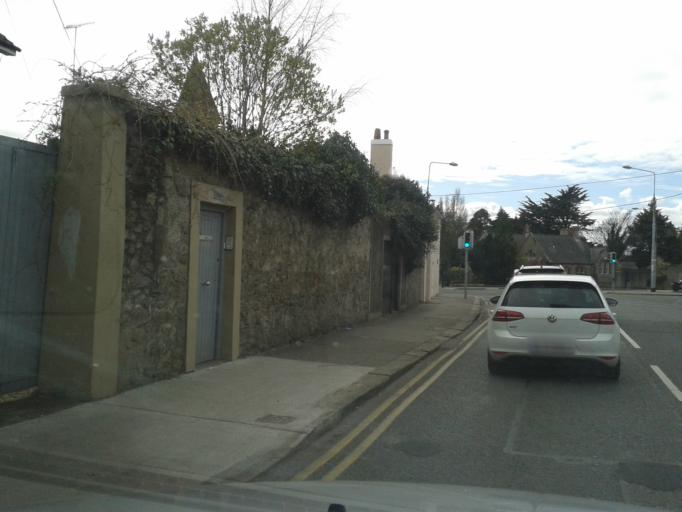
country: IE
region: Leinster
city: Monkstown
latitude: 53.2885
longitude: -6.1445
